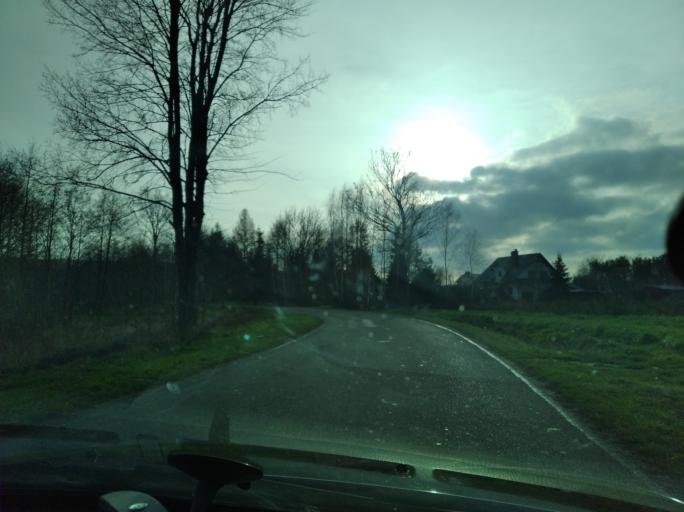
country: PL
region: Subcarpathian Voivodeship
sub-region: Powiat przeworski
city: Lopuszka Wielka
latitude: 49.9445
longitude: 22.4044
